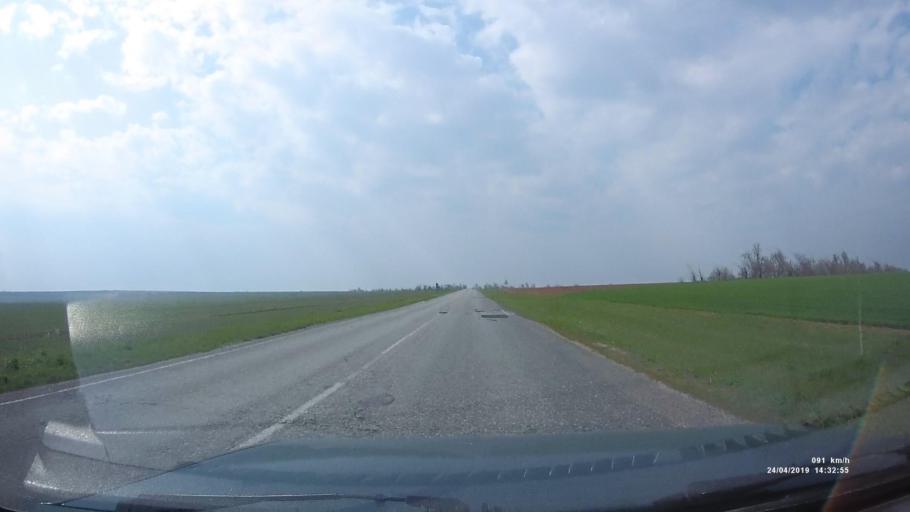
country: RU
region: Kalmykiya
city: Arshan'
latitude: 46.3683
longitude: 43.9626
